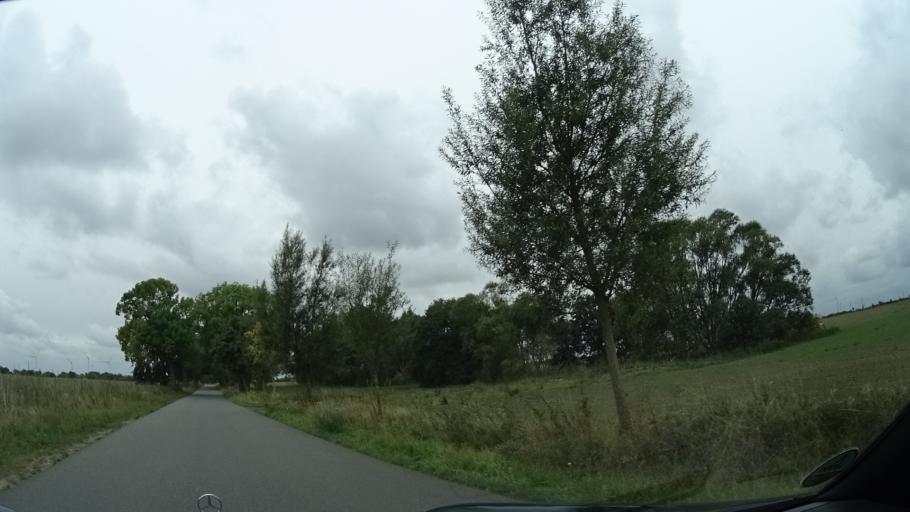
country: DE
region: Brandenburg
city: Dabergotz
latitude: 52.9400
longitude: 12.7503
